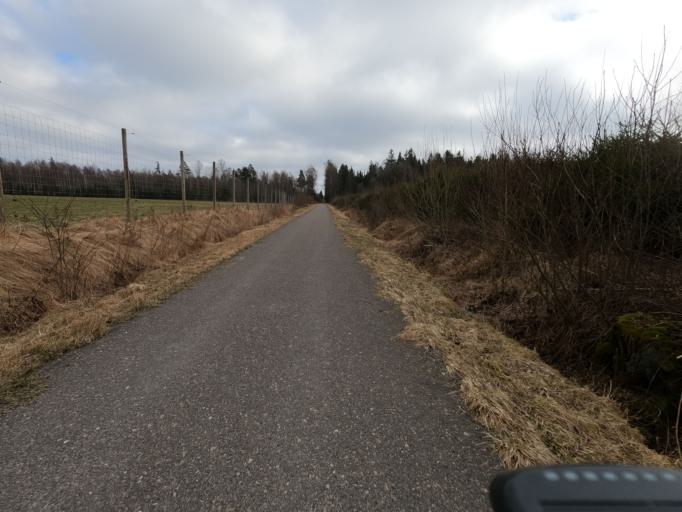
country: SE
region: Joenkoeping
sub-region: Varnamo Kommun
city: Rydaholm
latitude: 56.8607
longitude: 14.1744
